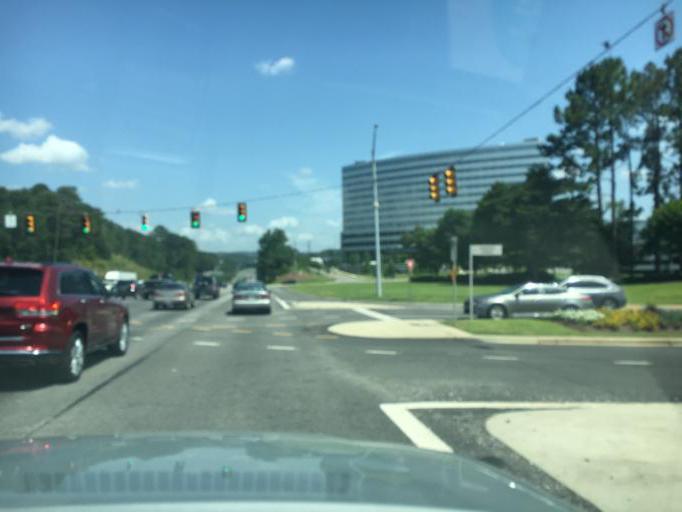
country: US
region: Alabama
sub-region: Jefferson County
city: Cahaba Heights
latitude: 33.4358
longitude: -86.7198
